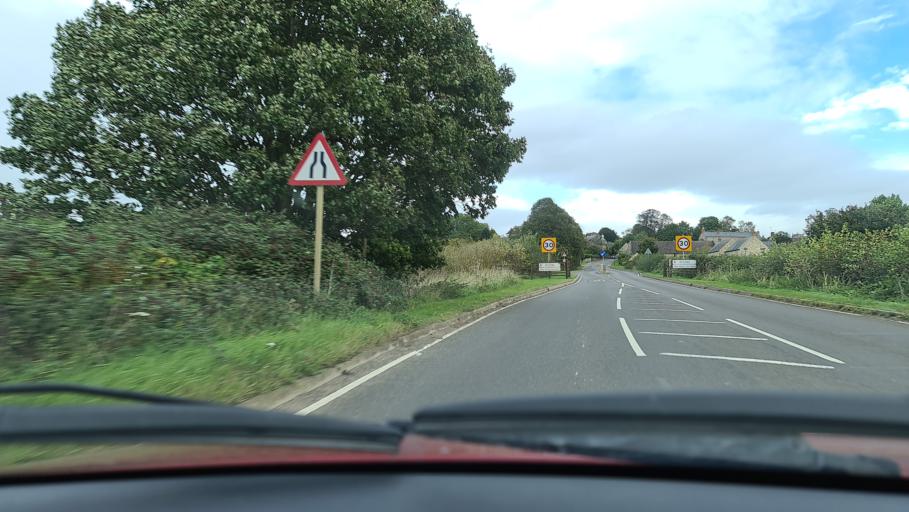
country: GB
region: England
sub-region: Oxfordshire
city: Somerton
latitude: 51.9970
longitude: -1.2594
